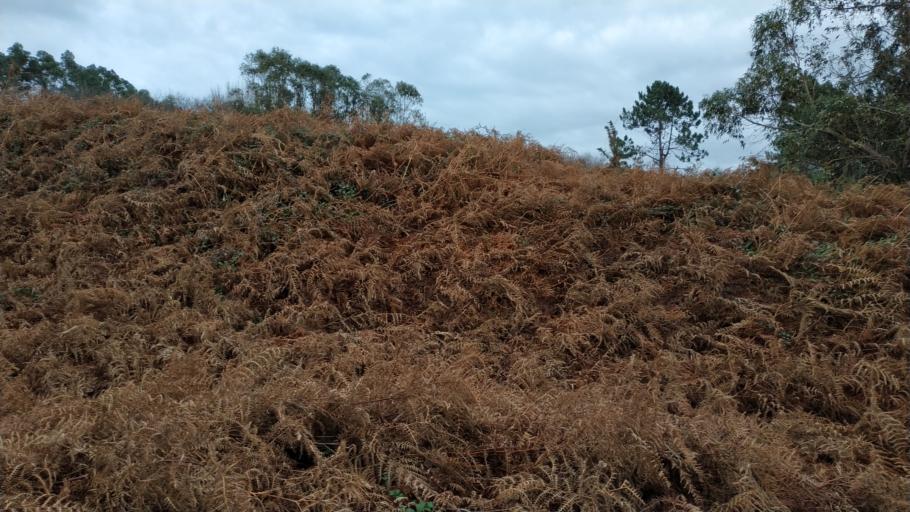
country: ES
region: Galicia
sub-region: Provincia da Coruna
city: Oleiros
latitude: 43.3998
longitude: -8.3296
